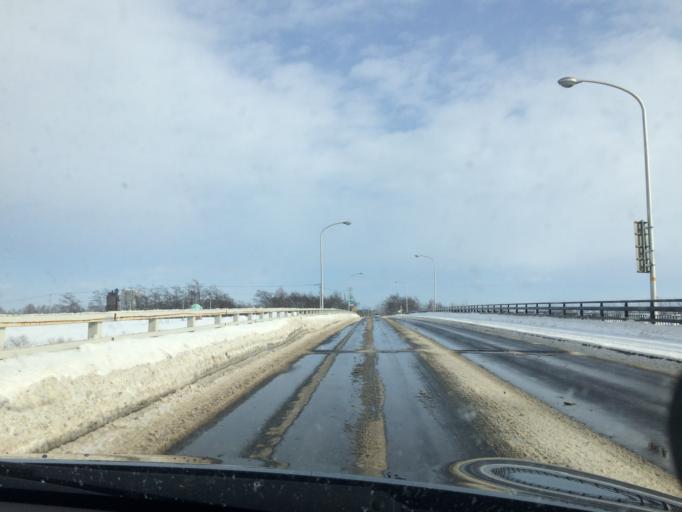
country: JP
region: Hokkaido
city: Kitahiroshima
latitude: 43.0176
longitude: 141.5784
